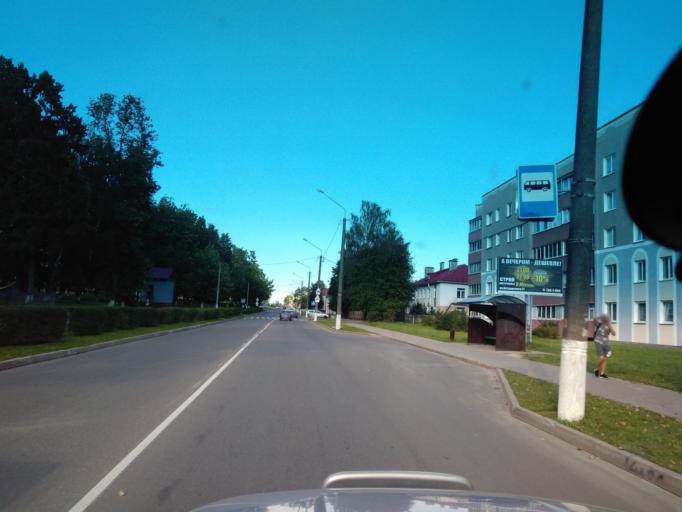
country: BY
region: Minsk
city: Dzyarzhynsk
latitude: 53.6826
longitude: 27.1264
